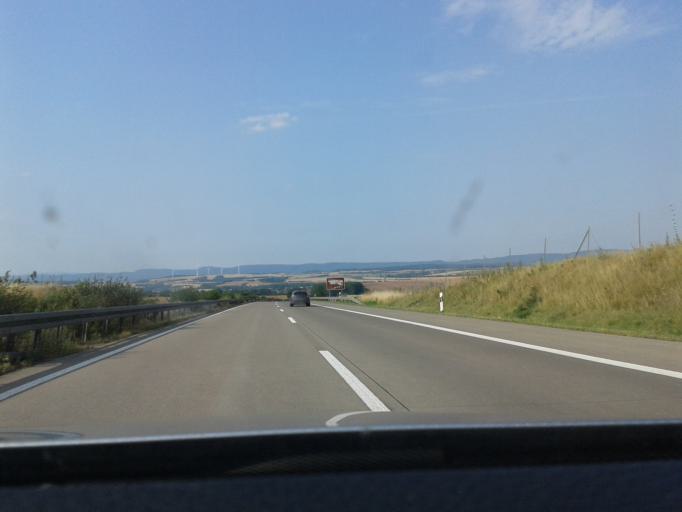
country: DE
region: Thuringia
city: Wipperdorf
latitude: 51.4672
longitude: 10.6882
